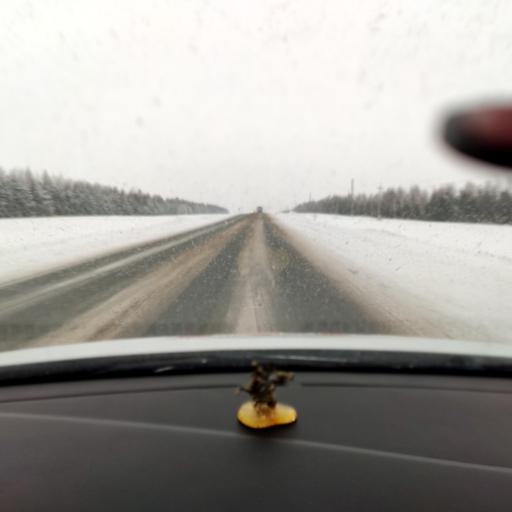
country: RU
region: Tatarstan
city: Vysokaya Gora
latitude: 56.0199
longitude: 49.2632
